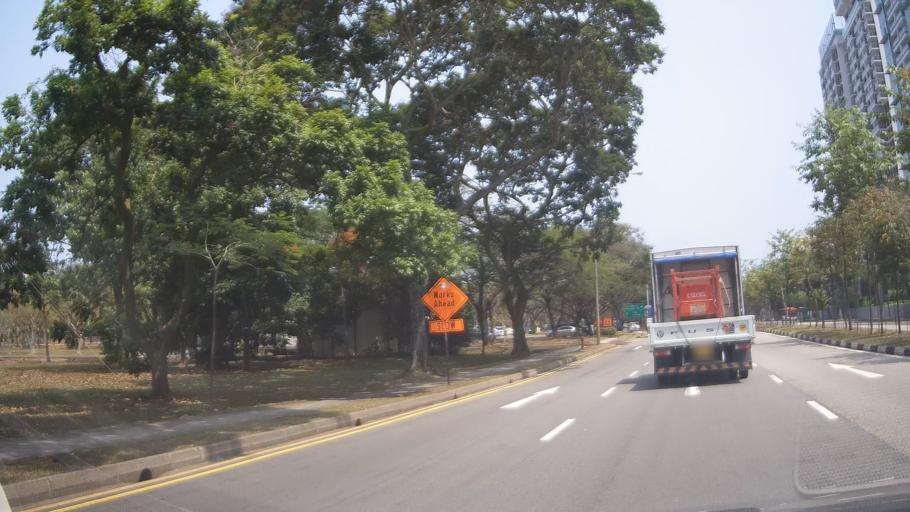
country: SG
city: Singapore
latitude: 1.2968
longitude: 103.7644
